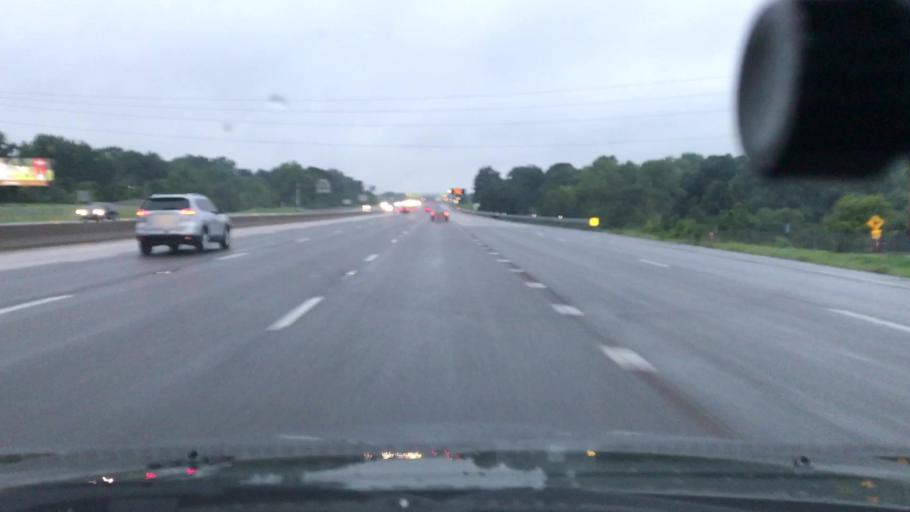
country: US
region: Missouri
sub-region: Saint Louis County
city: Creve Coeur
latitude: 38.6685
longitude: -90.4491
